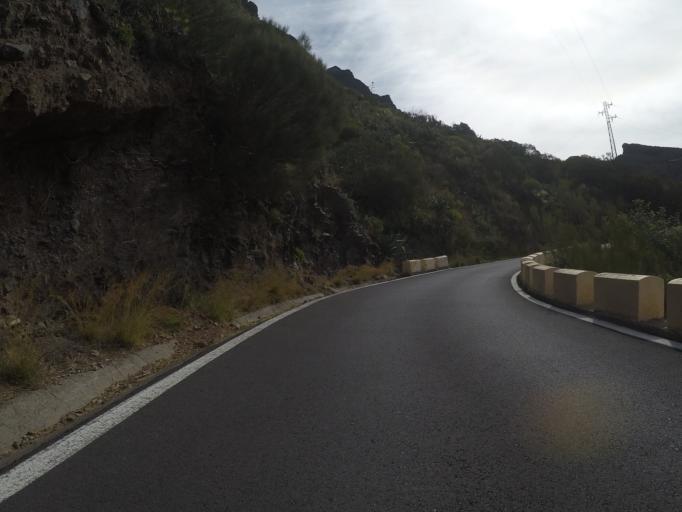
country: ES
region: Canary Islands
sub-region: Provincia de Santa Cruz de Tenerife
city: Santiago del Teide
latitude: 28.3041
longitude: -16.8373
